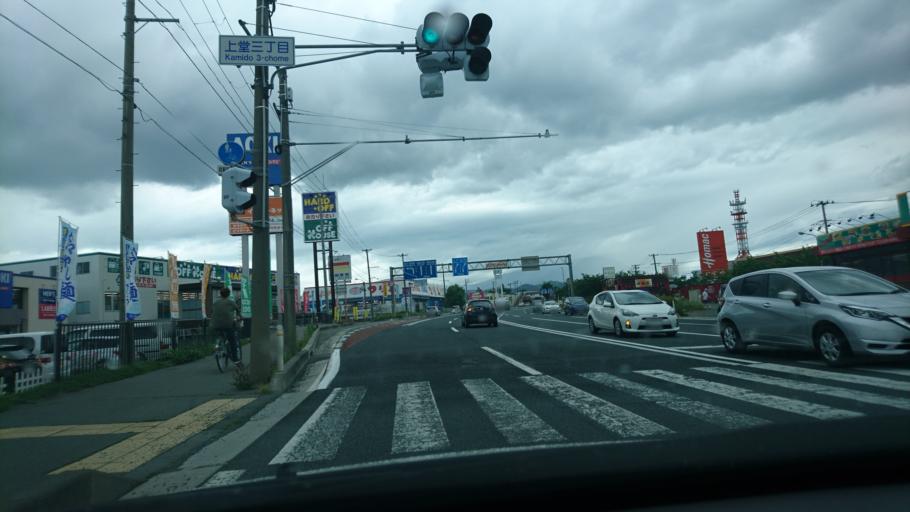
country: JP
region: Iwate
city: Morioka-shi
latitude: 39.7254
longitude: 141.1249
